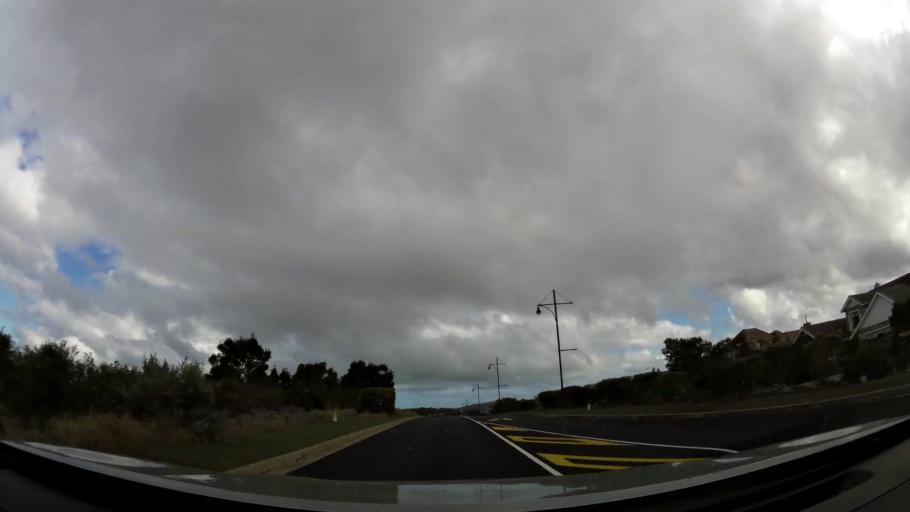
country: ZA
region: Western Cape
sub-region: Eden District Municipality
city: Knysna
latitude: -34.0662
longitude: 23.1010
